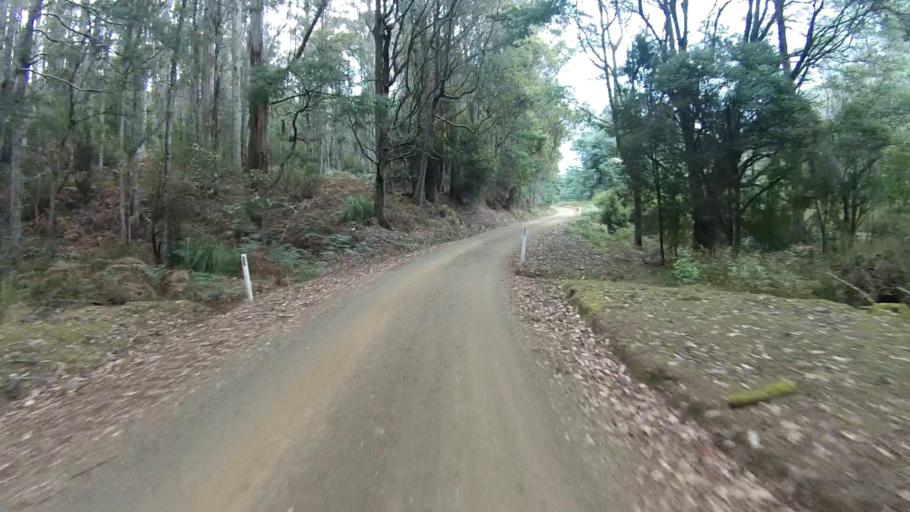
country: AU
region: Tasmania
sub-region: Kingborough
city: Kettering
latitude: -43.2129
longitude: 147.1787
